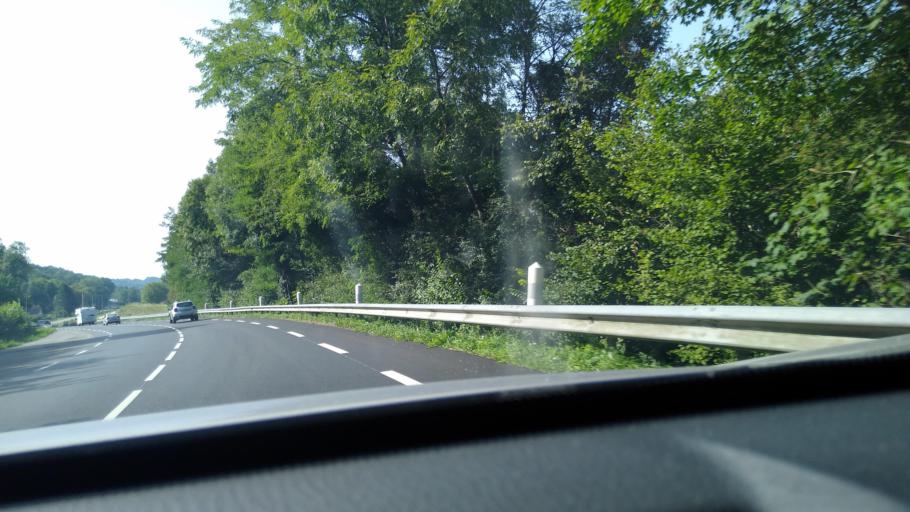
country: FR
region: Midi-Pyrenees
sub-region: Departement de la Haute-Garonne
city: Salies-du-Salat
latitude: 43.0721
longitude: 0.9660
